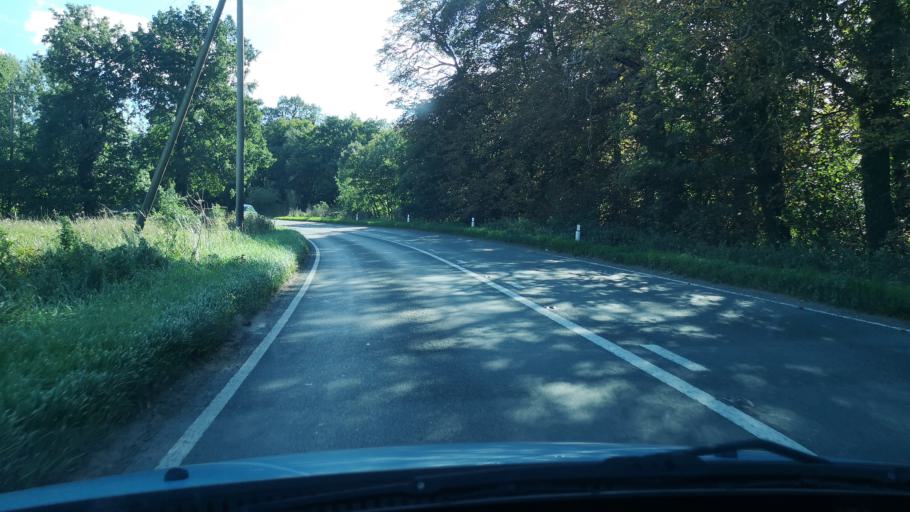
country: GB
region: England
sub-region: North Lincolnshire
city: Crowle
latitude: 53.5802
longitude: -0.8211
